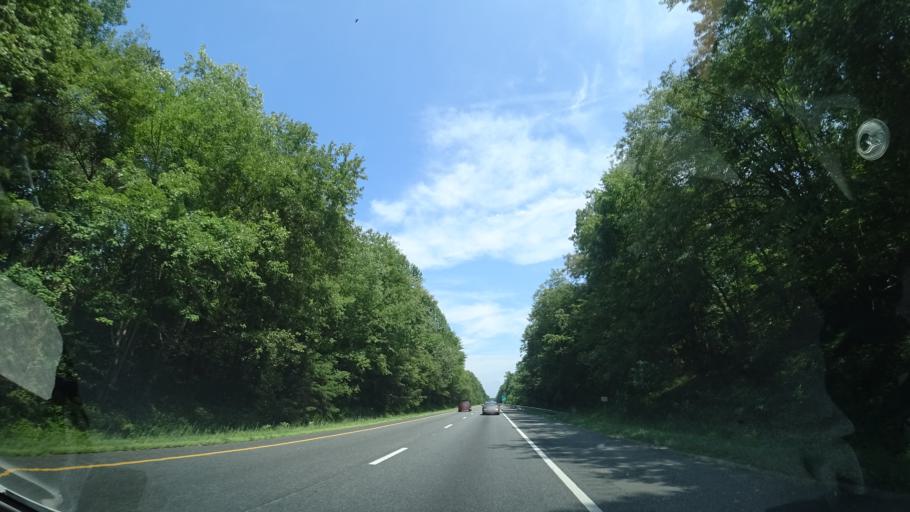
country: US
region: Virginia
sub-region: Fluvanna County
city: Lake Monticello
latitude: 38.0050
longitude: -78.3613
